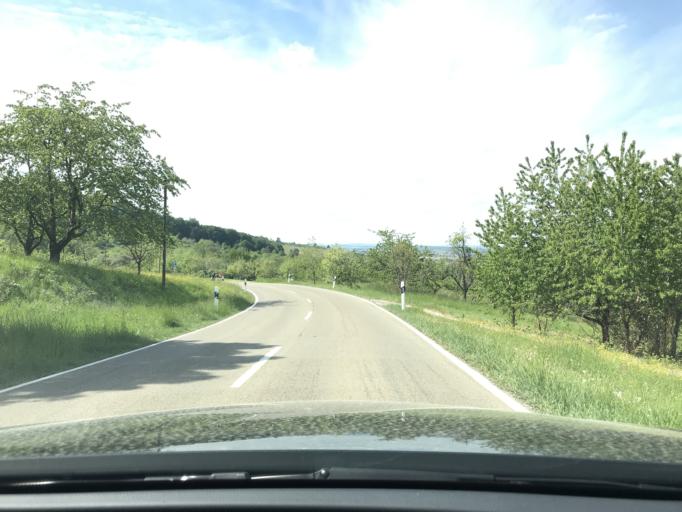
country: DE
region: Baden-Wuerttemberg
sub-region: Regierungsbezirk Stuttgart
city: Weinstadt-Endersbach
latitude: 48.7749
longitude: 9.3717
